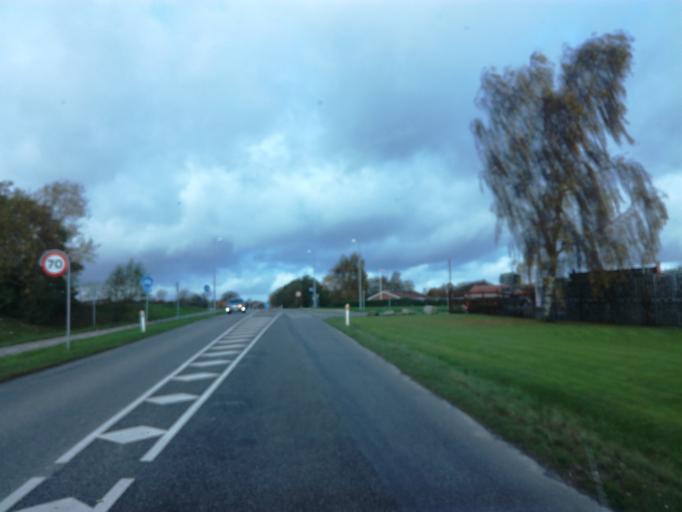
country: DK
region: South Denmark
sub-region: Vejle Kommune
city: Borkop
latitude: 55.6632
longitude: 9.6286
